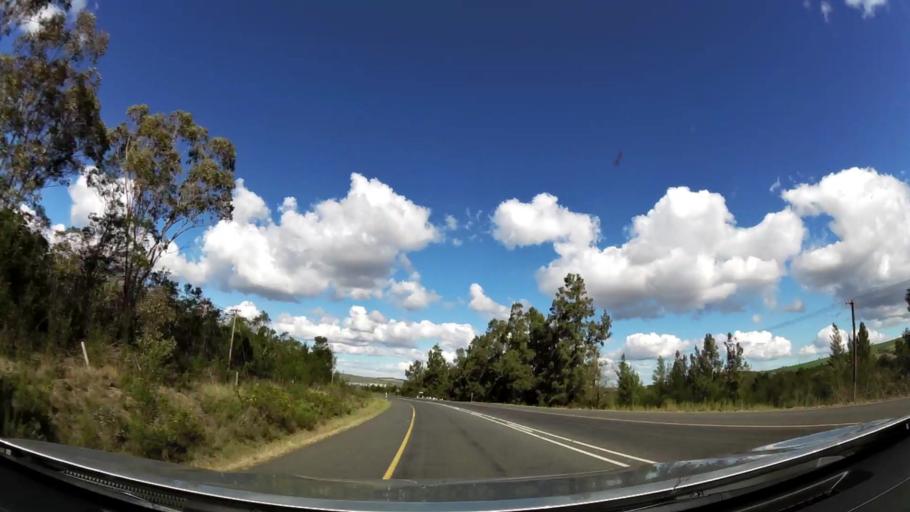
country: ZA
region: Western Cape
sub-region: Overberg District Municipality
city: Swellendam
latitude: -34.0306
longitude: 20.4203
